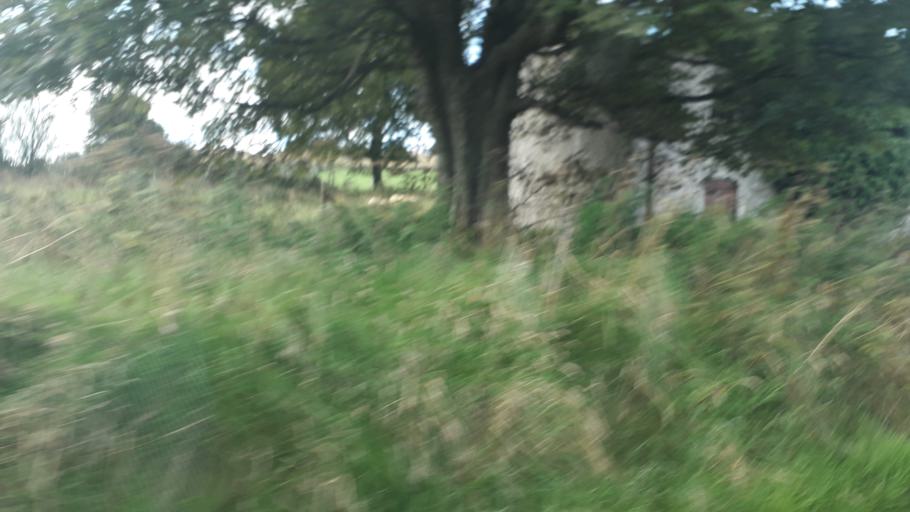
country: GB
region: Northern Ireland
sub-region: Down District
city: Warrenpoint
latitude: 54.0381
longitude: -6.2676
